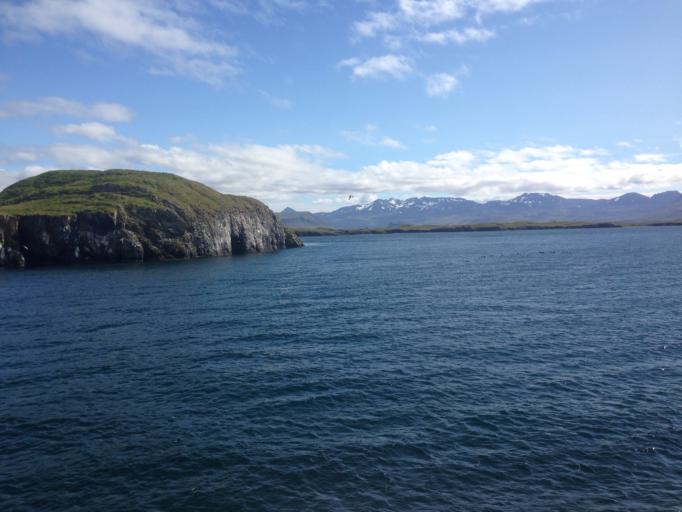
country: IS
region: West
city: Stykkisholmur
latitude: 65.0857
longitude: -22.6819
